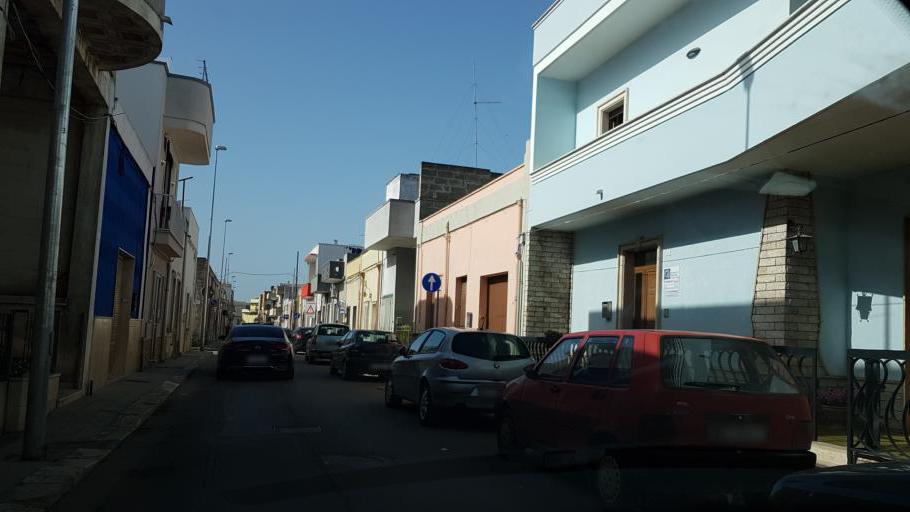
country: IT
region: Apulia
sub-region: Provincia di Brindisi
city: San Pancrazio Salentino
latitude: 40.4204
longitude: 17.8405
